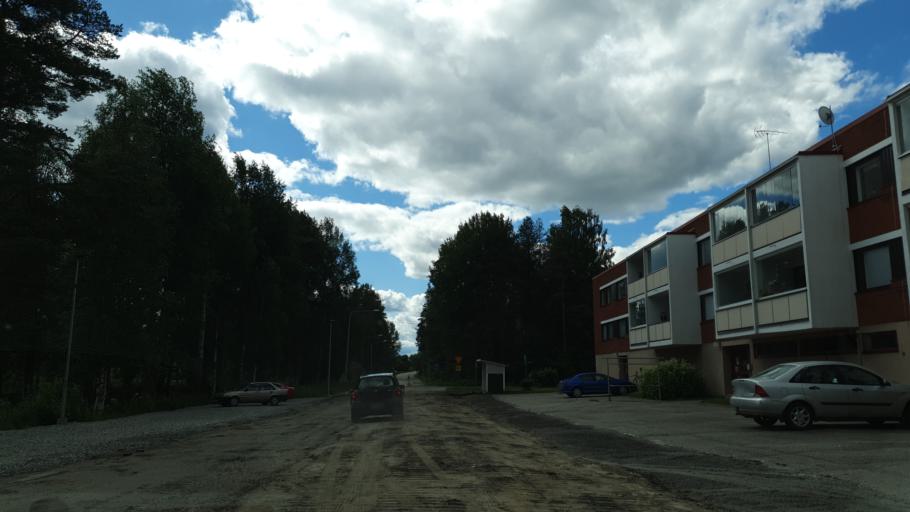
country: FI
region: Kainuu
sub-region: Kehys-Kainuu
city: Kuhmo
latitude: 64.1335
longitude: 29.5444
